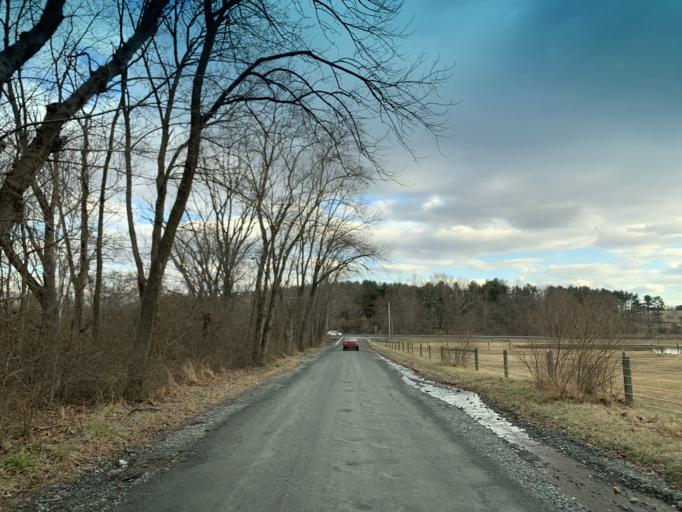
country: US
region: Maryland
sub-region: Harford County
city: South Bel Air
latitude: 39.5932
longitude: -76.2897
